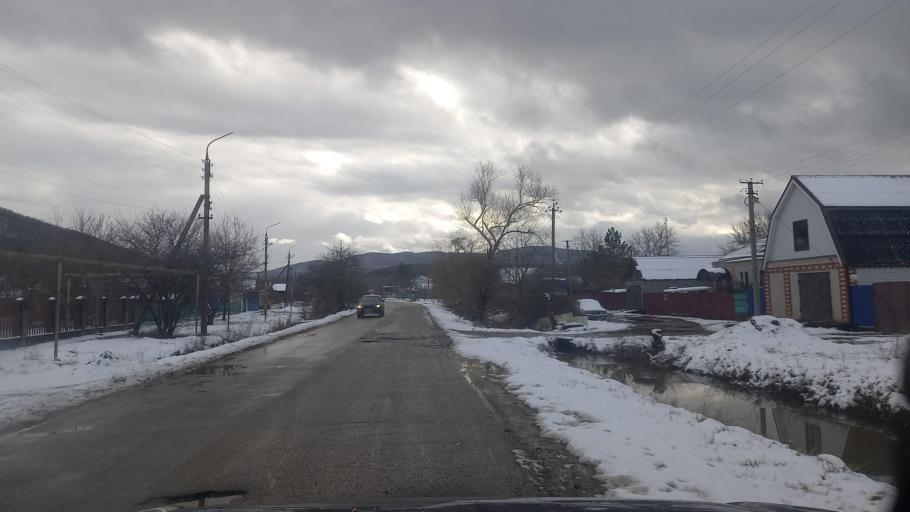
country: RU
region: Krasnodarskiy
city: Smolenskaya
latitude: 44.7170
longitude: 38.8251
